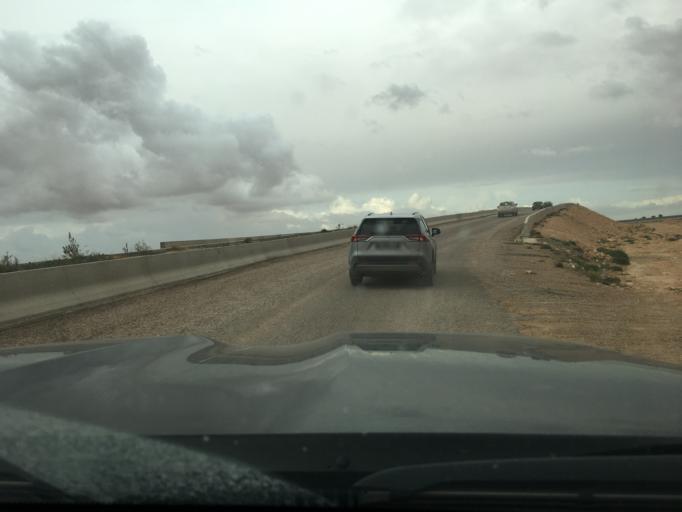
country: TN
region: Madanin
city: Medenine
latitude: 33.2977
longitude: 10.6085
